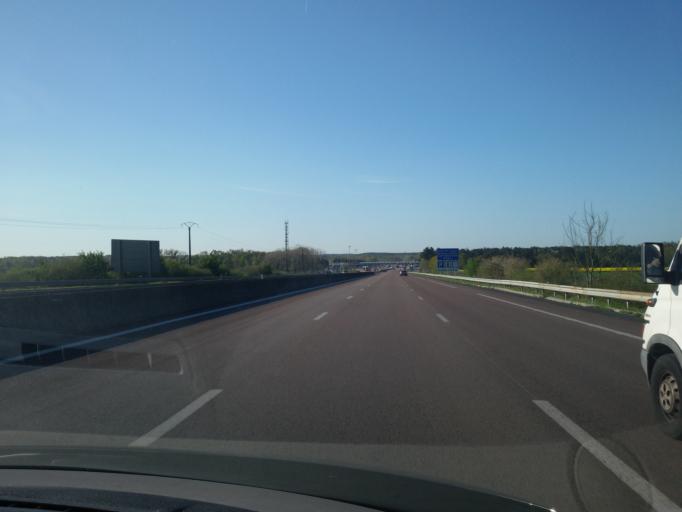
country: FR
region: Ile-de-France
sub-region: Departement de Seine-et-Marne
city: Cely
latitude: 48.4343
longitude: 2.5369
